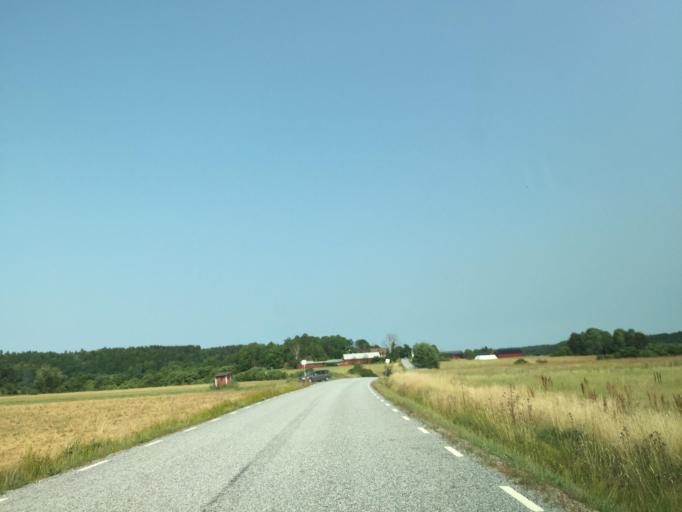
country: SE
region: Vaestra Goetaland
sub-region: Lilla Edets Kommun
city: Lilla Edet
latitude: 58.2076
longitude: 12.1292
